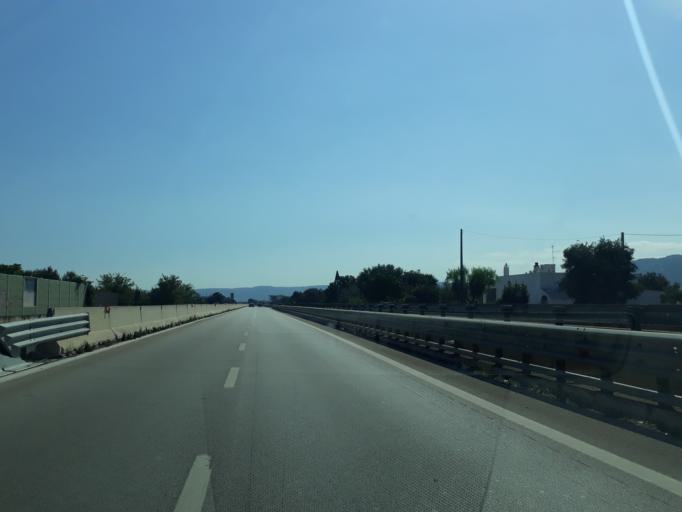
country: IT
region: Apulia
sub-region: Provincia di Brindisi
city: Fasano
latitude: 40.8673
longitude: 17.3449
